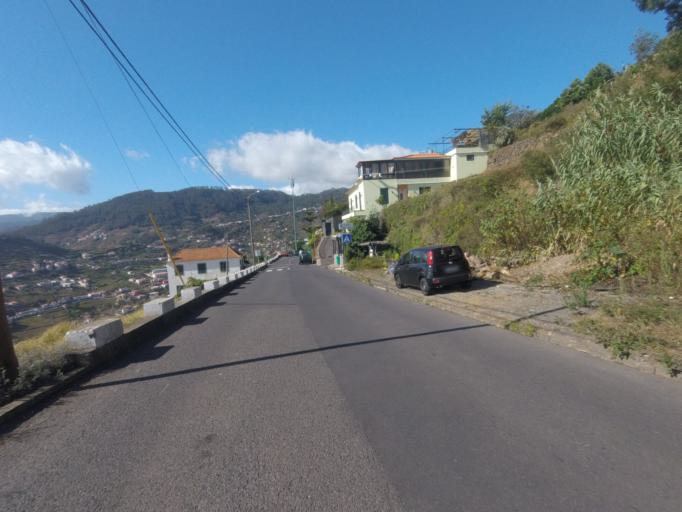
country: PT
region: Madeira
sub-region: Ribeira Brava
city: Campanario
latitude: 32.6650
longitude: -17.0240
